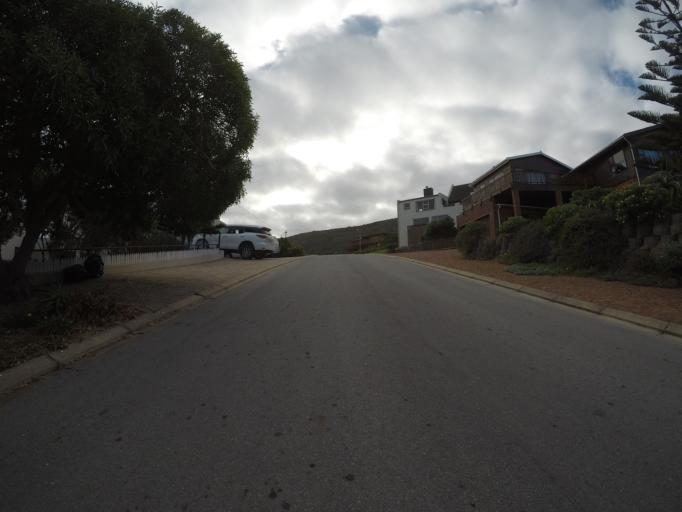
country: ZA
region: Western Cape
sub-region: Eden District Municipality
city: Riversdale
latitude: -34.4318
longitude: 21.3303
